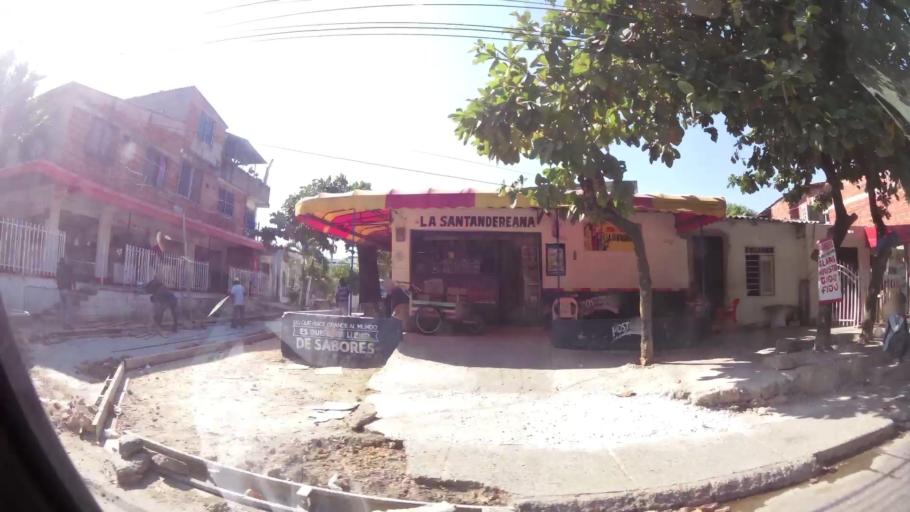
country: CO
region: Bolivar
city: Cartagena
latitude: 10.3989
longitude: -75.5004
